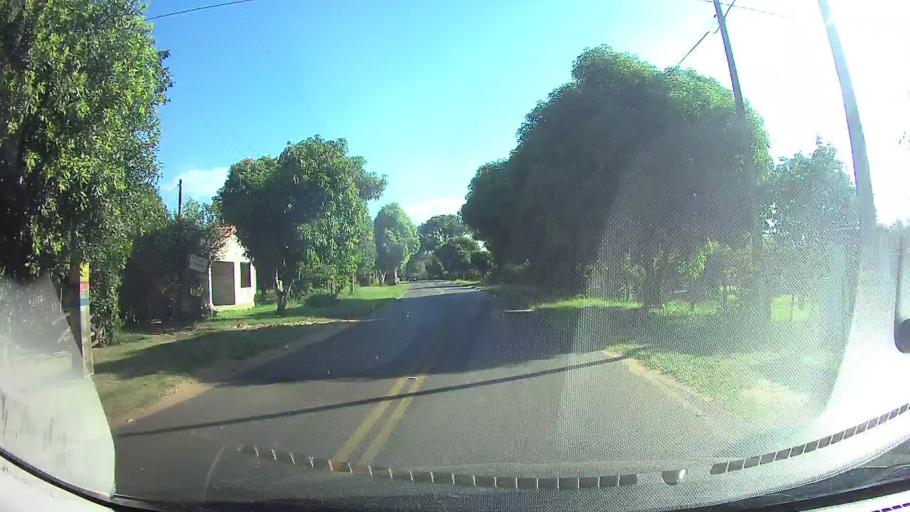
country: PY
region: Cordillera
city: Atyra
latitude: -25.2946
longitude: -57.1842
